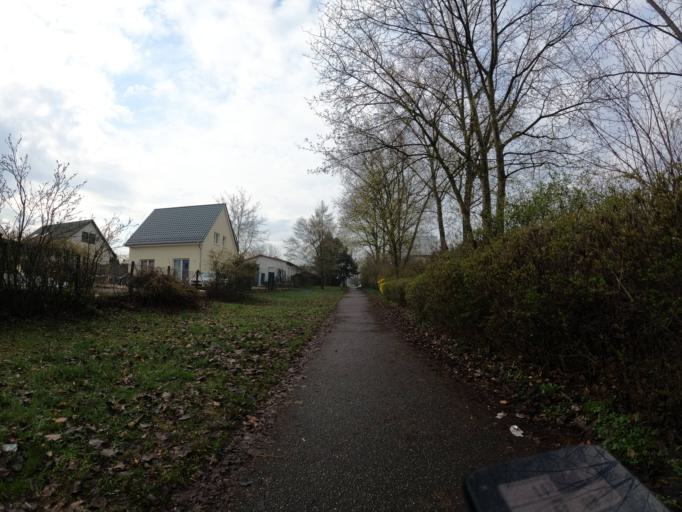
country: DE
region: Berlin
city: Marzahn
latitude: 52.5329
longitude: 13.5554
